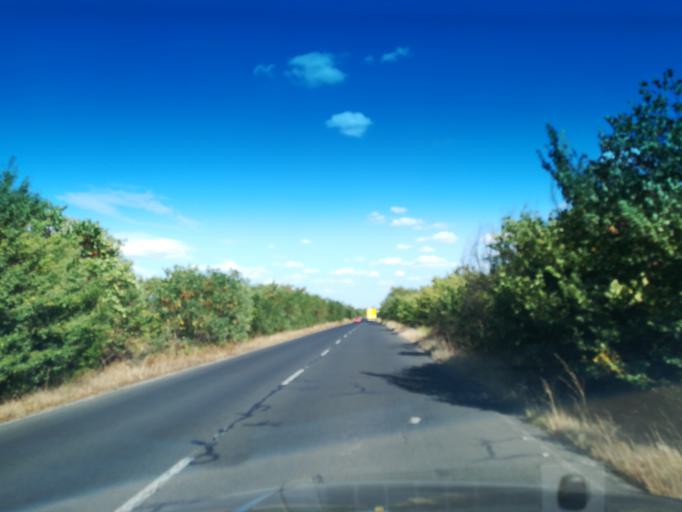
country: BG
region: Khaskovo
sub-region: Obshtina Mineralni Bani
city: Mineralni Bani
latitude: 42.0557
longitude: 25.3017
